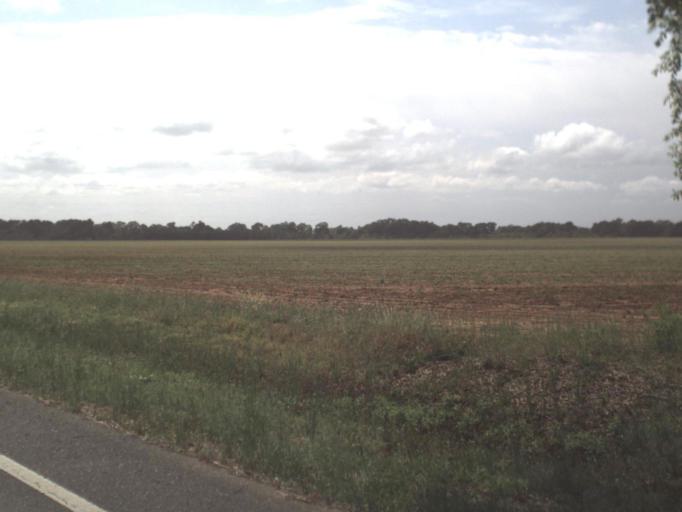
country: US
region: Alabama
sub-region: Escambia County
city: East Brewton
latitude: 30.9784
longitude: -87.1229
